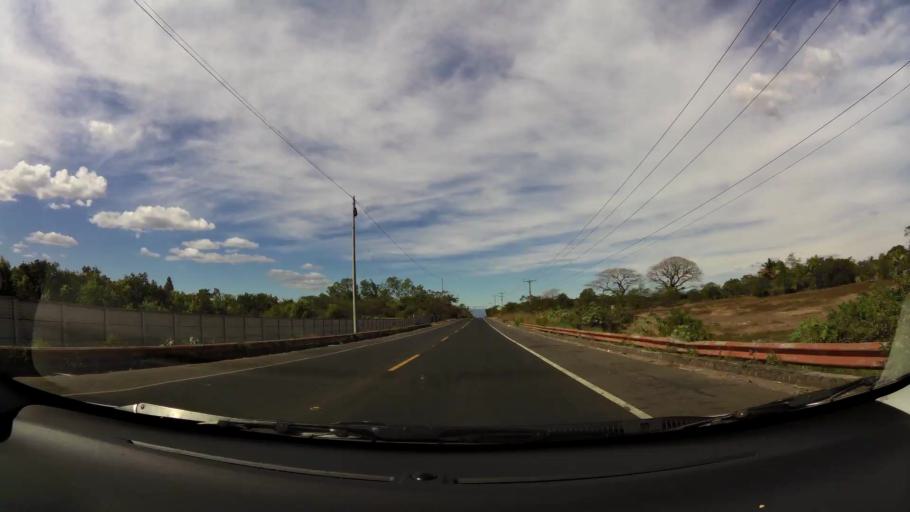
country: SV
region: San Salvador
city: Guazapa
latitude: 13.8918
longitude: -89.1770
